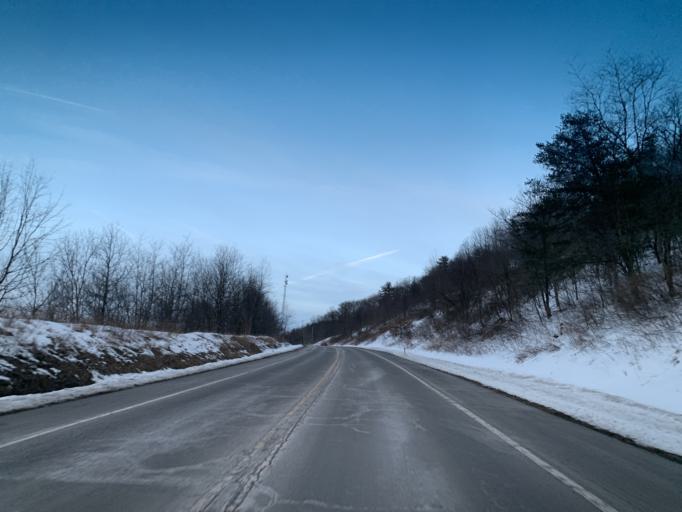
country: US
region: Maryland
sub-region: Allegany County
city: Cumberland
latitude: 39.6965
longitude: -78.6382
